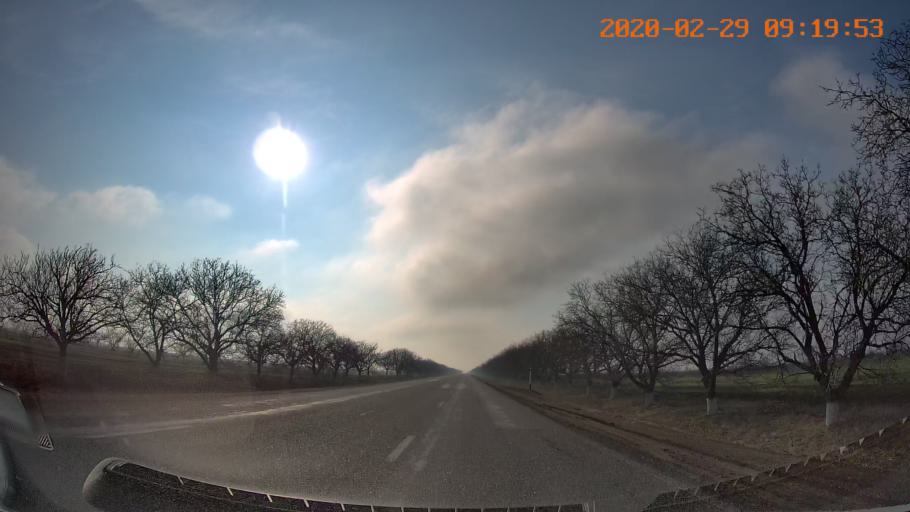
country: MD
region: Telenesti
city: Pervomaisc
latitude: 46.7568
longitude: 29.9432
